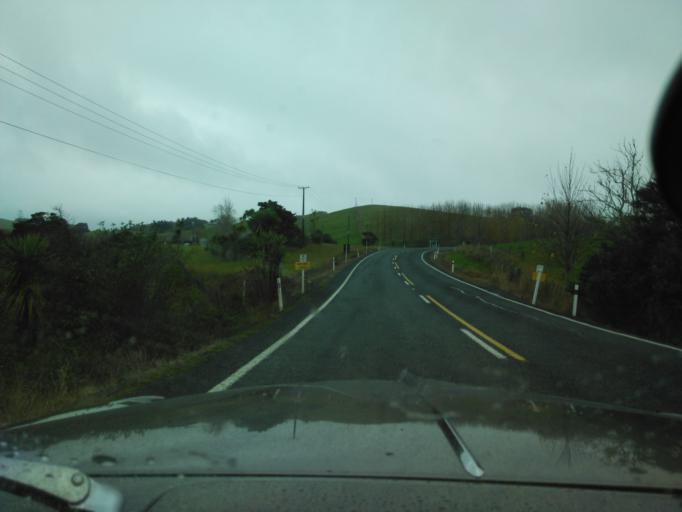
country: NZ
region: Auckland
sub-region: Auckland
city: Wellsford
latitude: -36.3790
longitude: 174.4511
